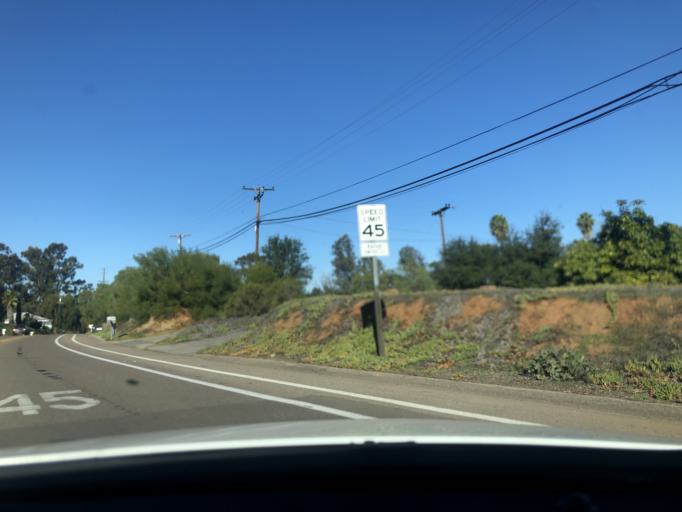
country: US
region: California
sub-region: San Diego County
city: Rancho San Diego
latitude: 32.7718
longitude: -116.9397
